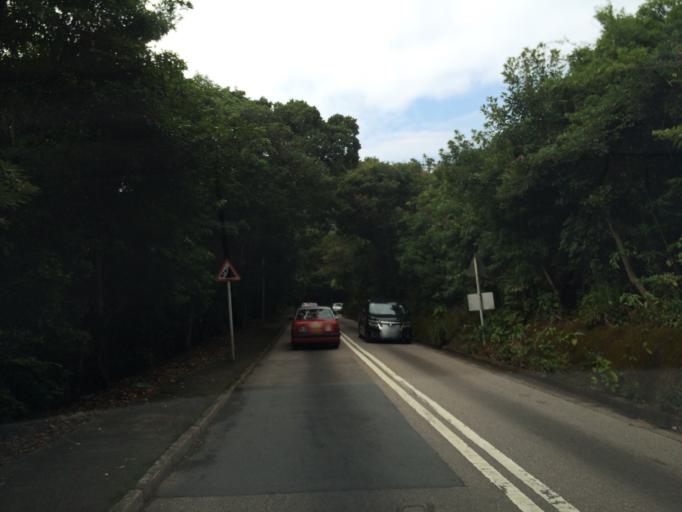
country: HK
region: Wanchai
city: Wan Chai
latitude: 22.2623
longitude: 114.2291
